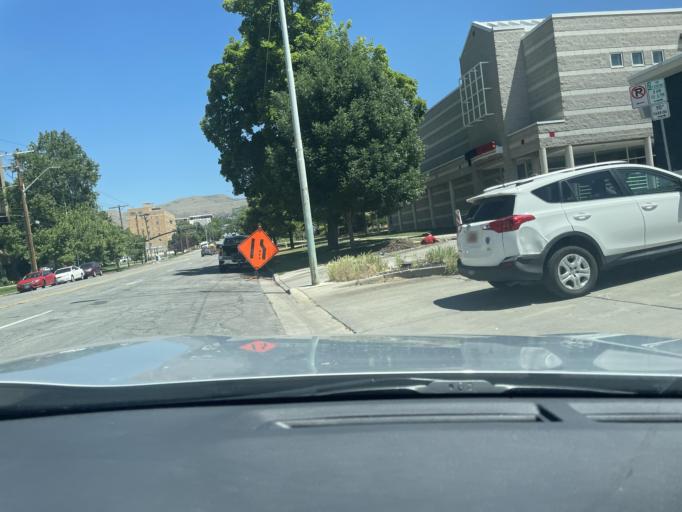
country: US
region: Utah
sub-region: Salt Lake County
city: Salt Lake City
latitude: 40.7637
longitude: -111.8767
